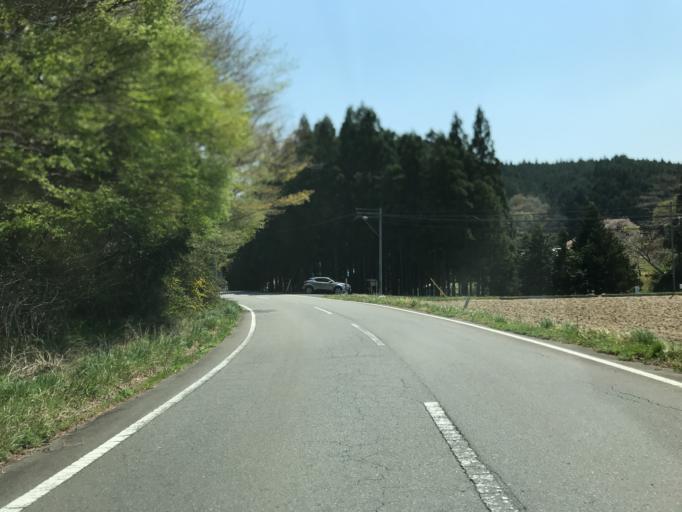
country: JP
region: Ibaraki
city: Kitaibaraki
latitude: 36.9594
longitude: 140.6674
